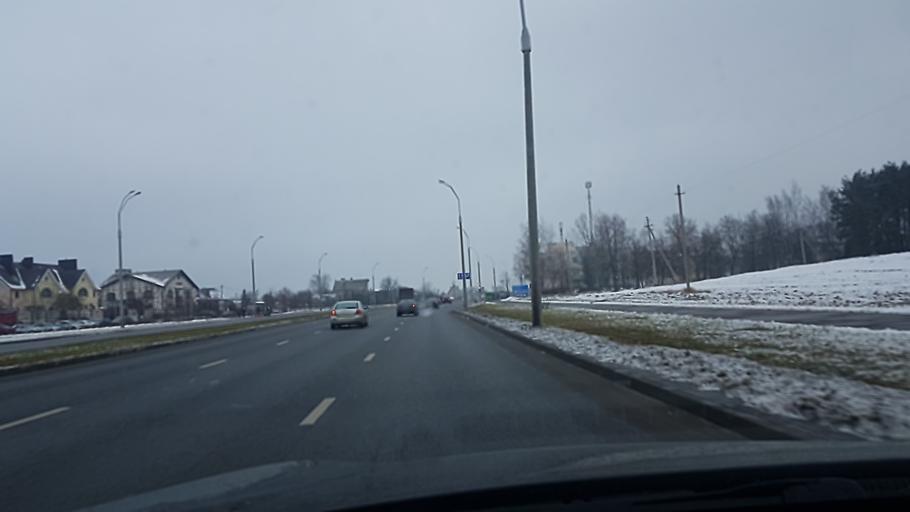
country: BY
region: Minsk
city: Minsk
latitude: 53.9511
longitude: 27.5355
